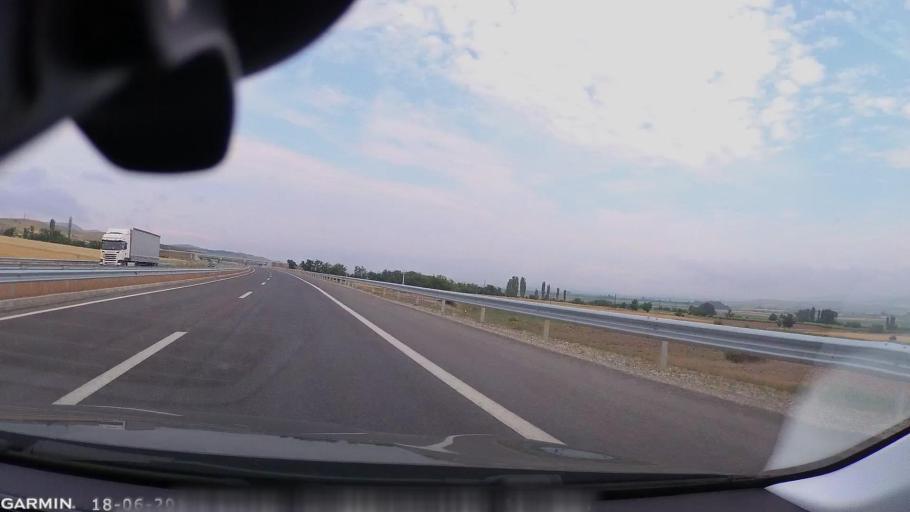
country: MK
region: Stip
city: Shtip
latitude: 41.7892
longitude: 22.1119
